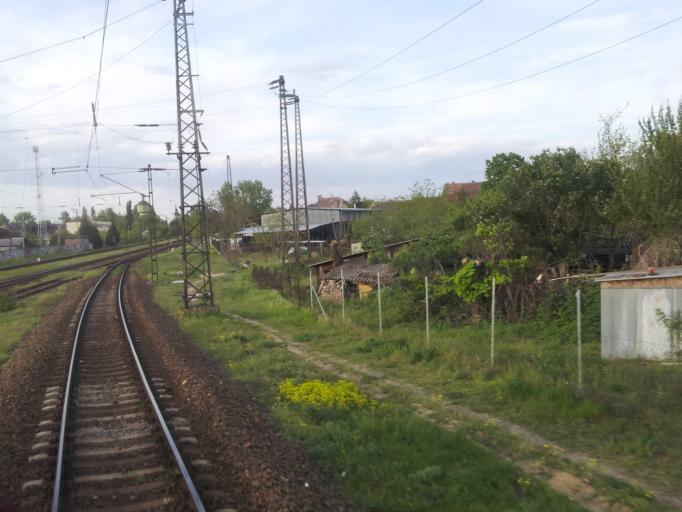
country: HU
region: Budapest
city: Budapest XV. keruelet
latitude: 47.5444
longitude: 19.1044
